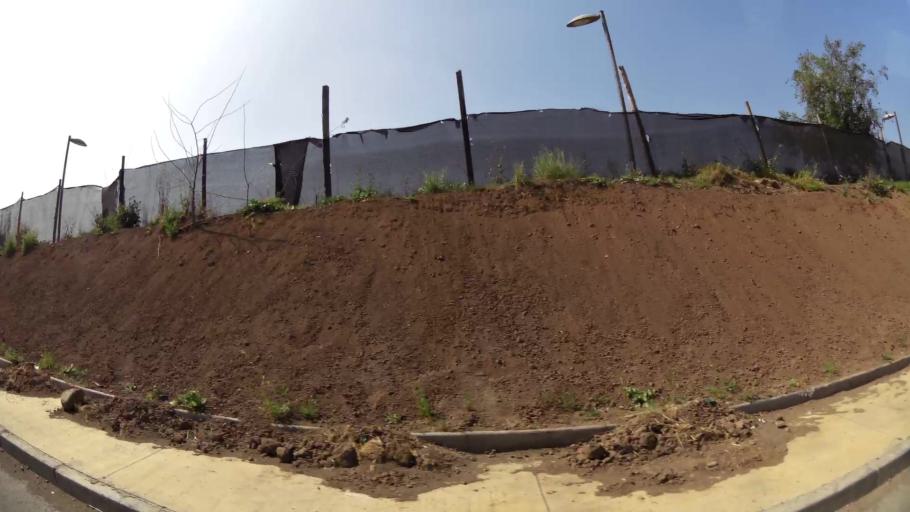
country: CL
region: Santiago Metropolitan
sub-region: Provincia de Santiago
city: Villa Presidente Frei, Nunoa, Santiago, Chile
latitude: -33.4042
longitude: -70.6028
